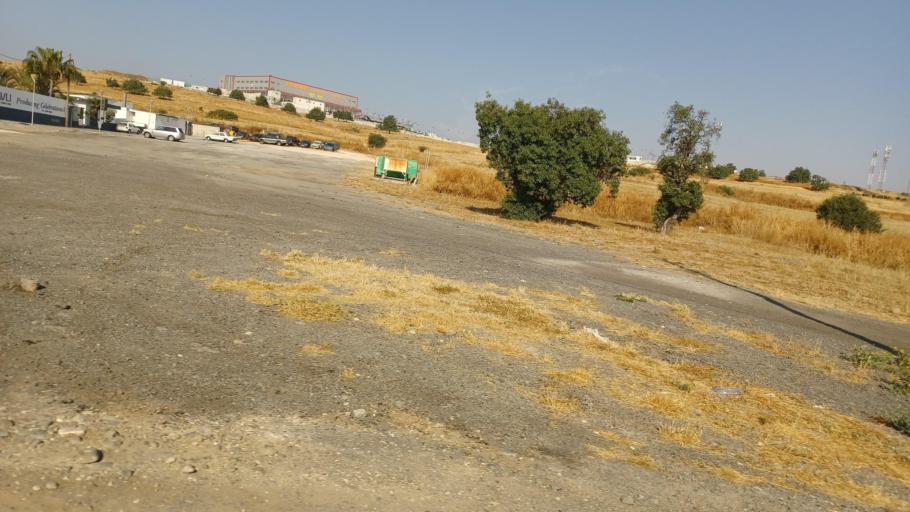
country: CY
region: Lefkosia
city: Lympia
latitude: 34.9882
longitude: 33.4666
